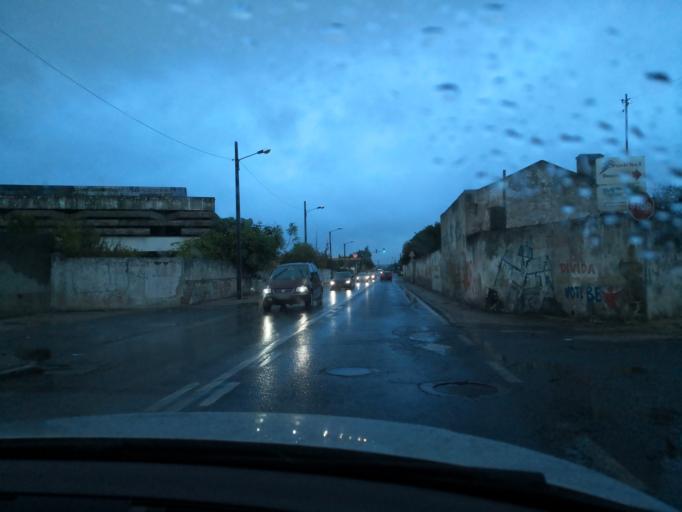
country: PT
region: Setubal
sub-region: Moita
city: Alhos Vedros
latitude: 38.6531
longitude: -9.0226
